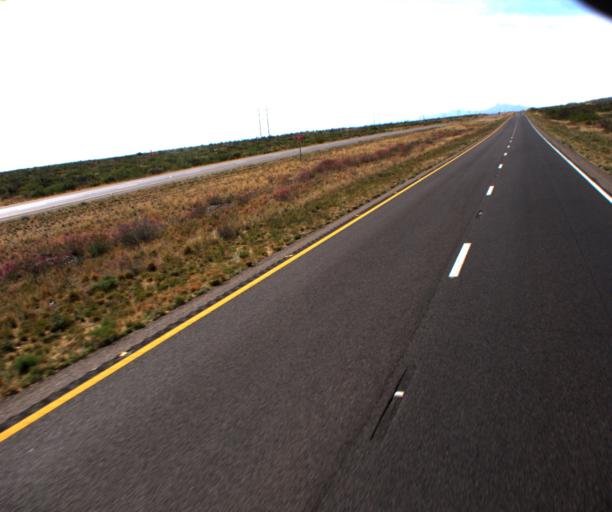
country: US
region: Arizona
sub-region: Graham County
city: Swift Trail Junction
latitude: 32.5765
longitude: -109.6820
